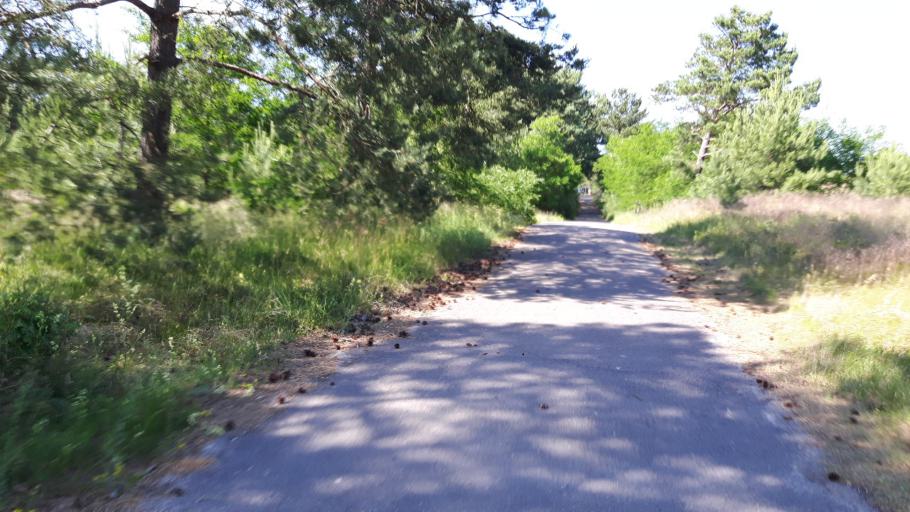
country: LT
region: Klaipedos apskritis
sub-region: Klaipeda
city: Klaipeda
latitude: 55.6923
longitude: 21.1030
